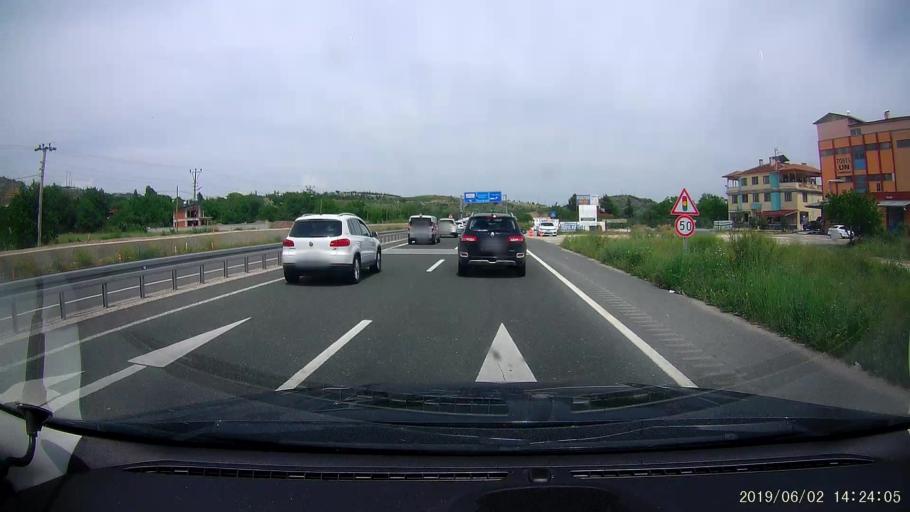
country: TR
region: Kastamonu
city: Tosya
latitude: 41.0007
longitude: 34.0298
